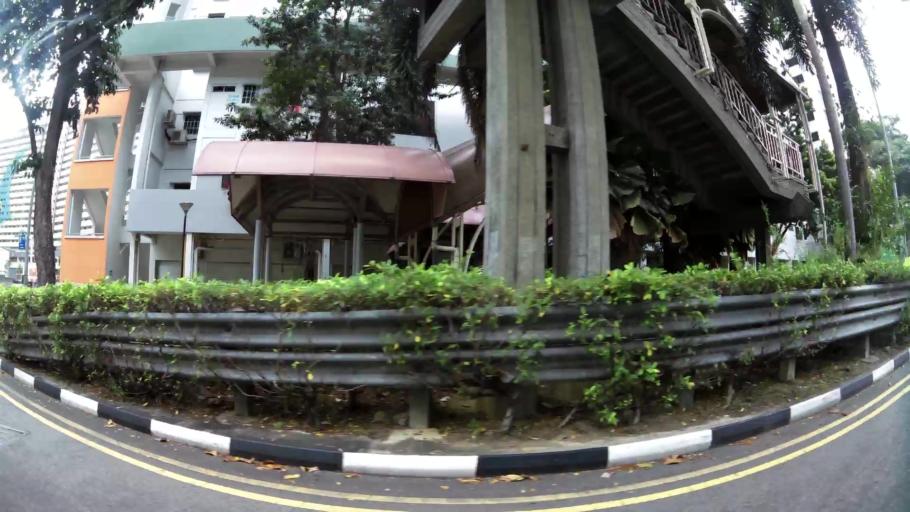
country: SG
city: Singapore
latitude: 1.2876
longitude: 103.8424
